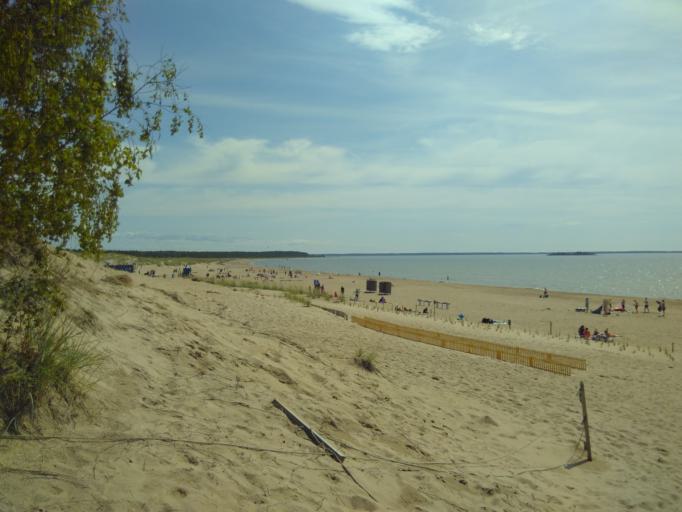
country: FI
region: Satakunta
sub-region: Pori
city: Luvia
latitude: 61.5672
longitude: 21.5197
